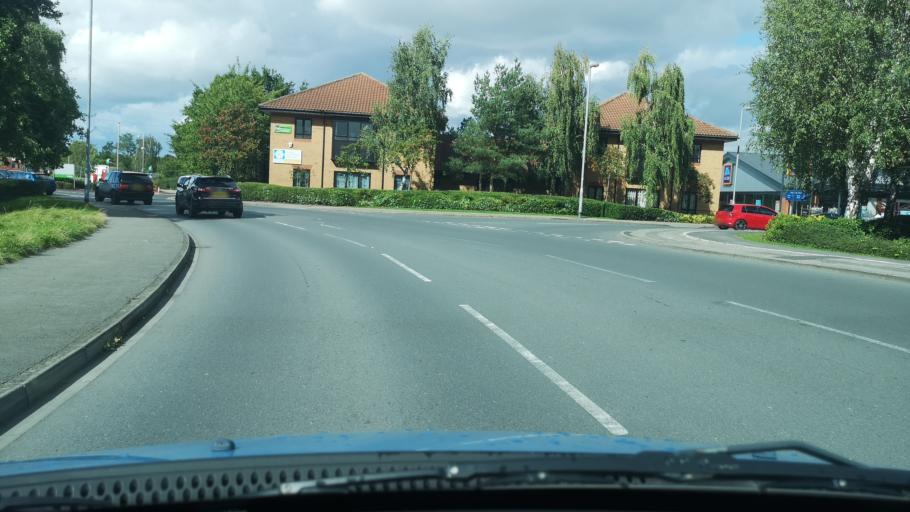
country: GB
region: England
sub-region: City and Borough of Wakefield
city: Crigglestone
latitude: 53.6492
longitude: -1.4980
